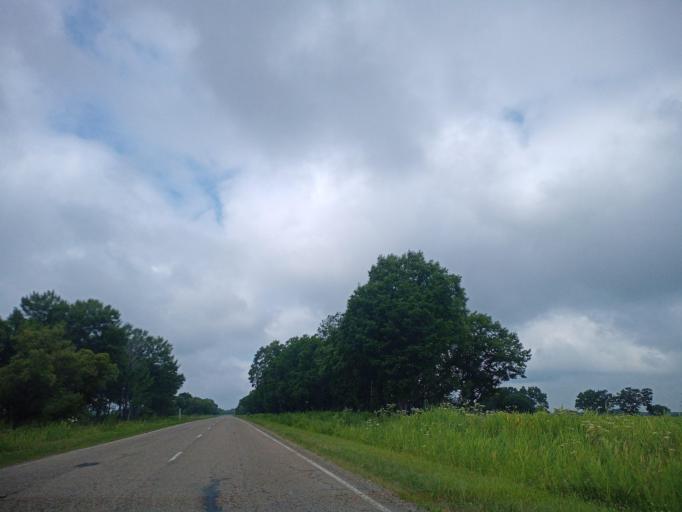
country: RU
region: Primorskiy
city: Dal'nerechensk
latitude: 45.9478
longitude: 133.9006
